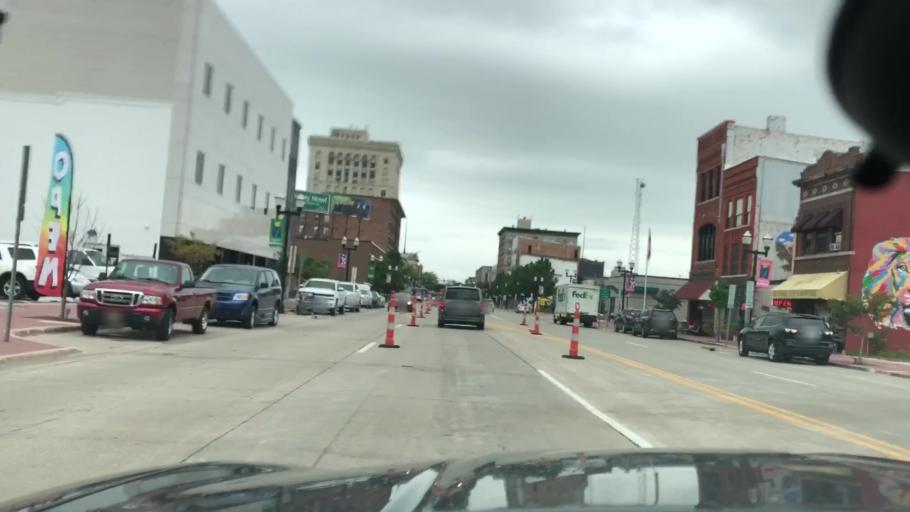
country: US
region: Michigan
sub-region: Saginaw County
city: Saginaw
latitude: 43.4312
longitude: -83.9398
